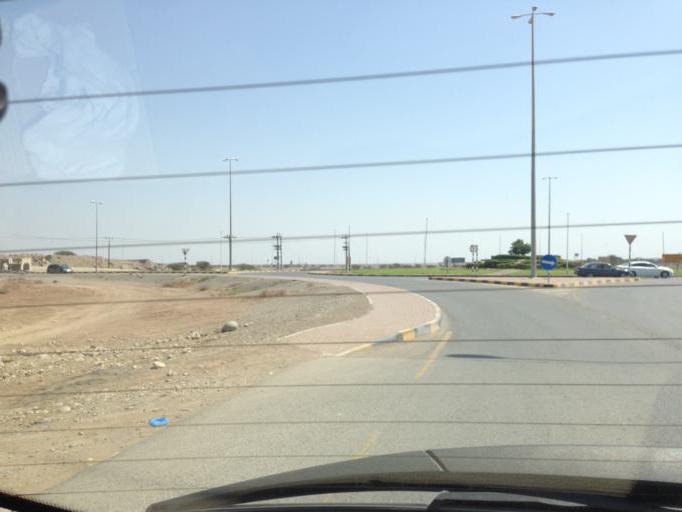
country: OM
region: Al Batinah
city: Rustaq
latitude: 23.5585
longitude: 57.4859
